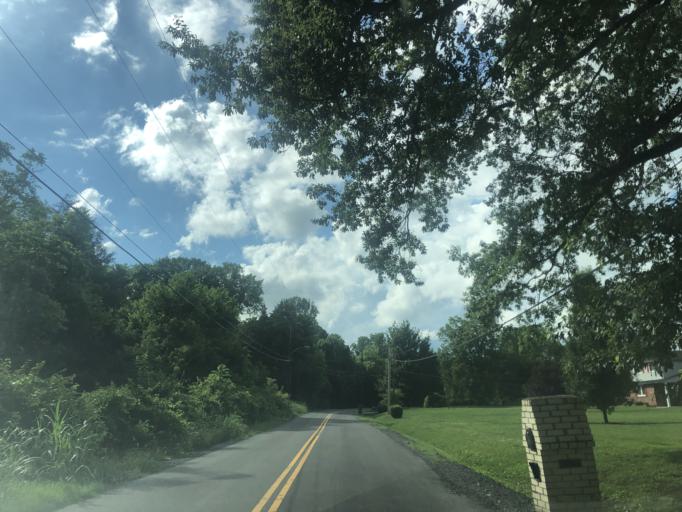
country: US
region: Tennessee
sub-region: Davidson County
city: Nashville
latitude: 36.2218
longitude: -86.8513
